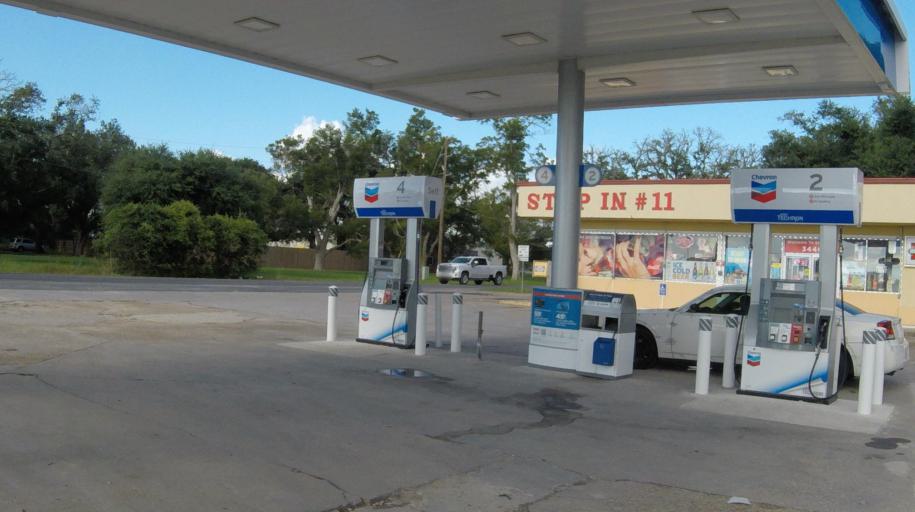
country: US
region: Louisiana
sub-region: Calcasieu Parish
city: Carlyss
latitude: 30.2021
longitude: -93.3764
